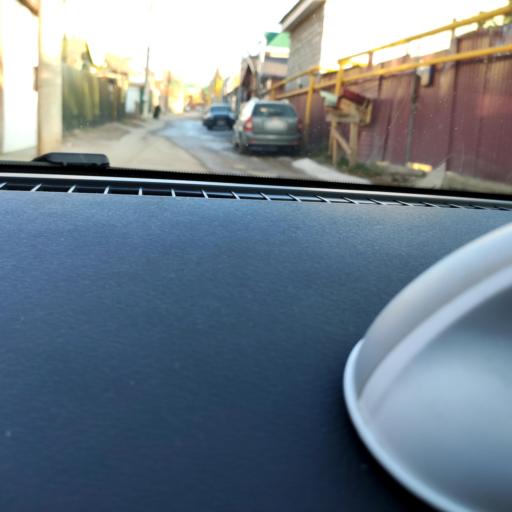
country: RU
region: Samara
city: Samara
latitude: 53.2273
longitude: 50.1619
